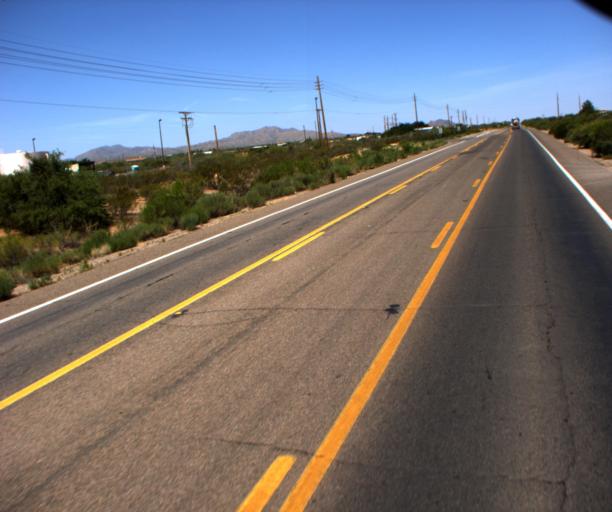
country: US
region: Arizona
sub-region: Gila County
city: Peridot
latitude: 33.3025
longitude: -110.4745
